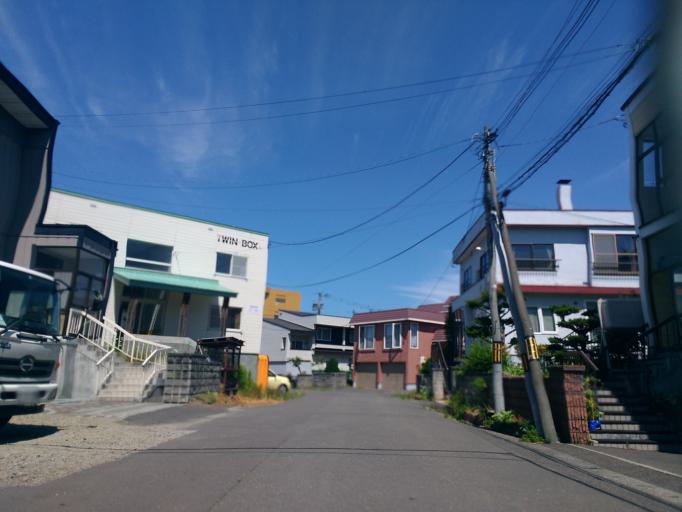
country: JP
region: Hokkaido
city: Ebetsu
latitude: 43.0678
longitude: 141.4928
